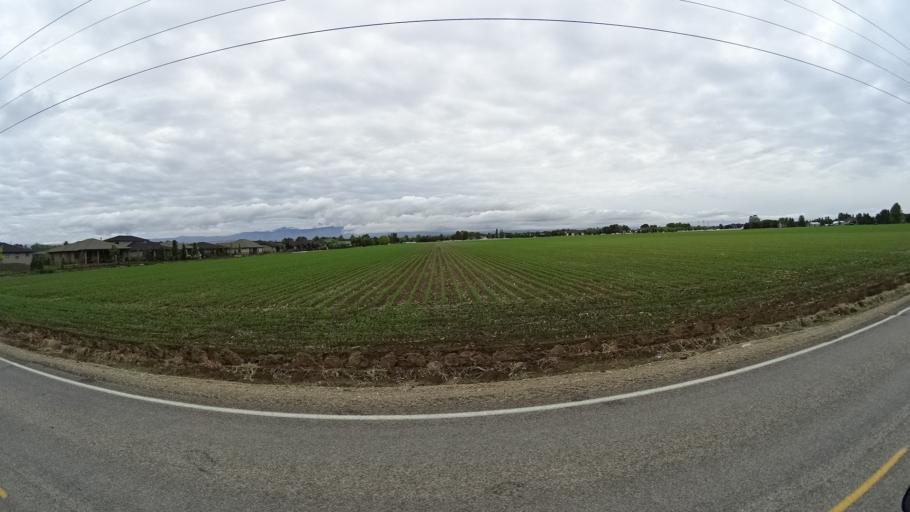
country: US
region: Idaho
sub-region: Ada County
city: Eagle
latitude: 43.7094
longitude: -116.4137
